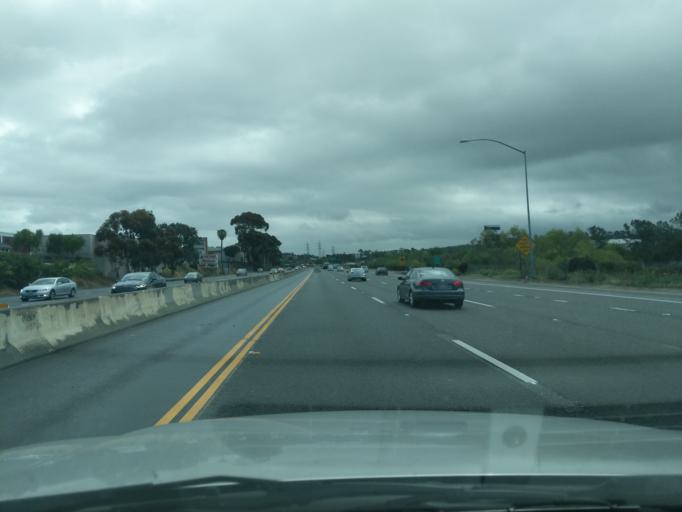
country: US
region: California
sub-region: San Diego County
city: Carlsbad
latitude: 33.1811
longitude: -117.3352
